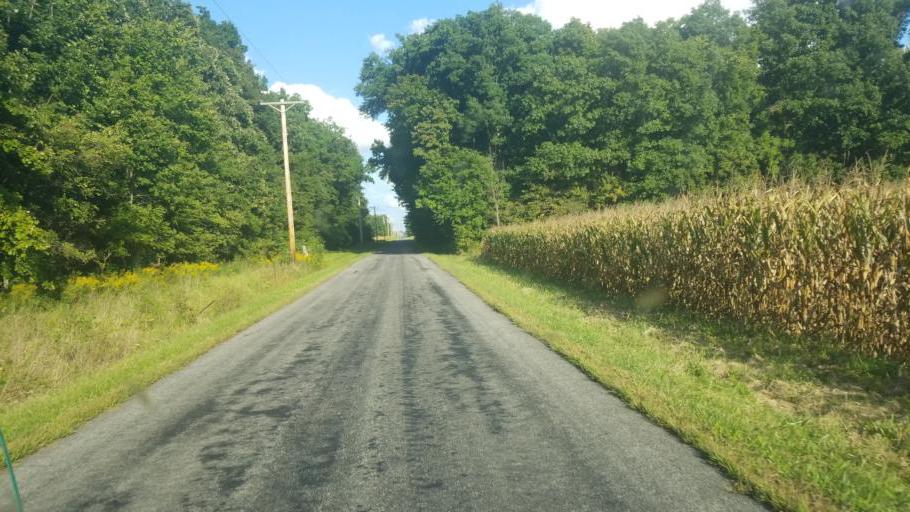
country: US
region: Ohio
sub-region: Hancock County
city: Arlington
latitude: 40.9362
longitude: -83.7208
